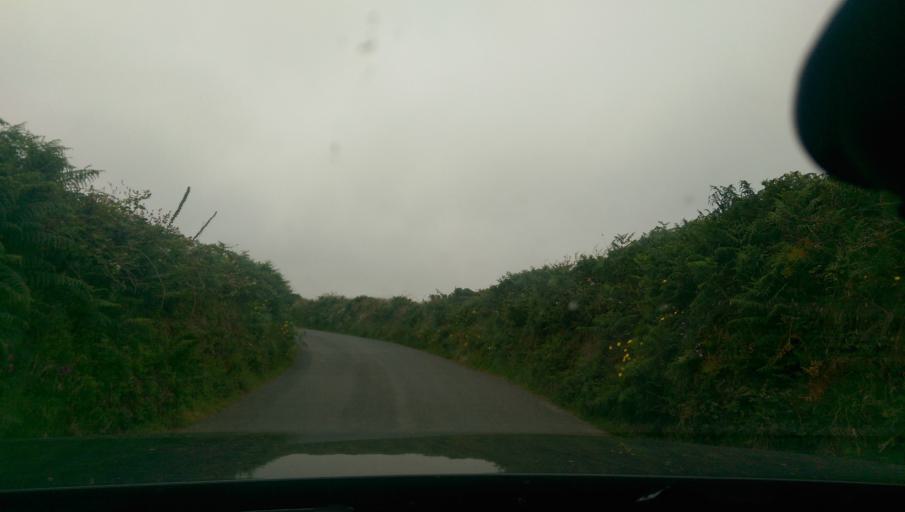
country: GB
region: England
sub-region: Cornwall
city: St. Buryan
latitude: 50.0959
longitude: -5.6494
